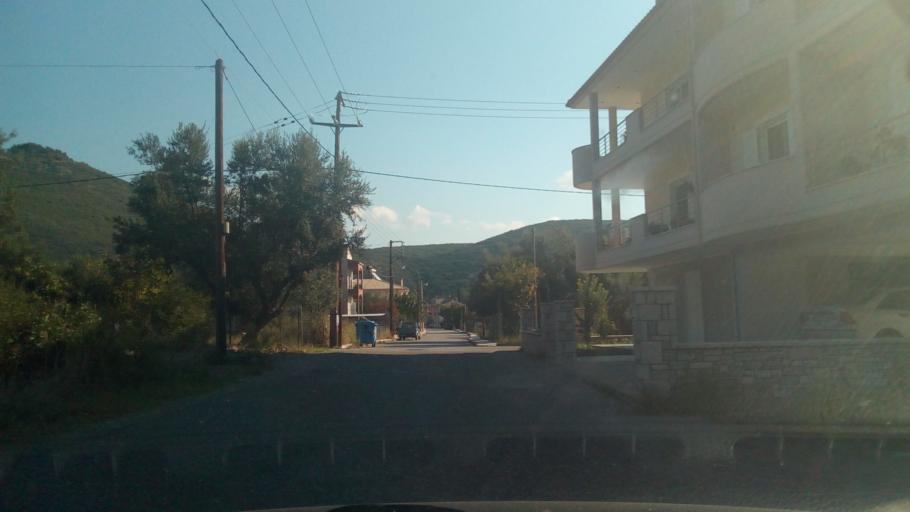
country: GR
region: West Greece
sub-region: Nomos Aitolias kai Akarnanias
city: Nafpaktos
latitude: 38.4066
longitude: 21.8476
